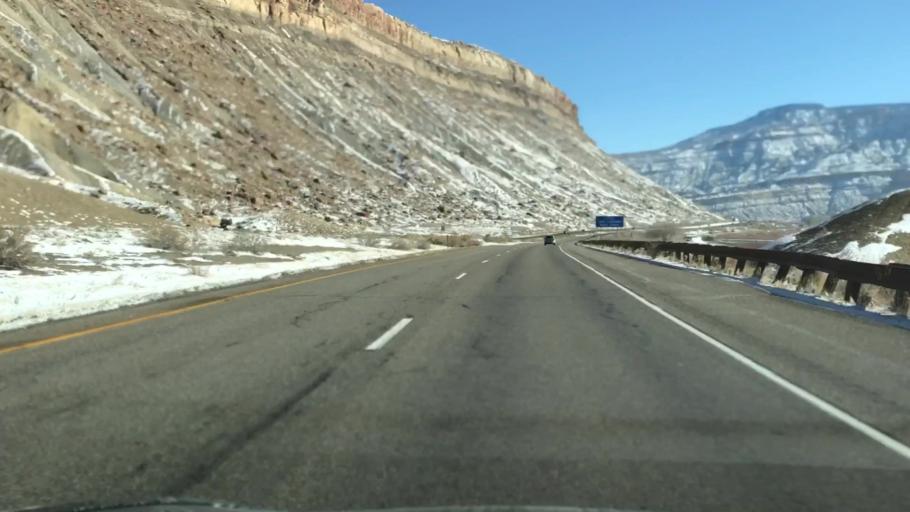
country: US
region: Colorado
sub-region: Mesa County
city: Palisade
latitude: 39.1204
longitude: -108.3730
